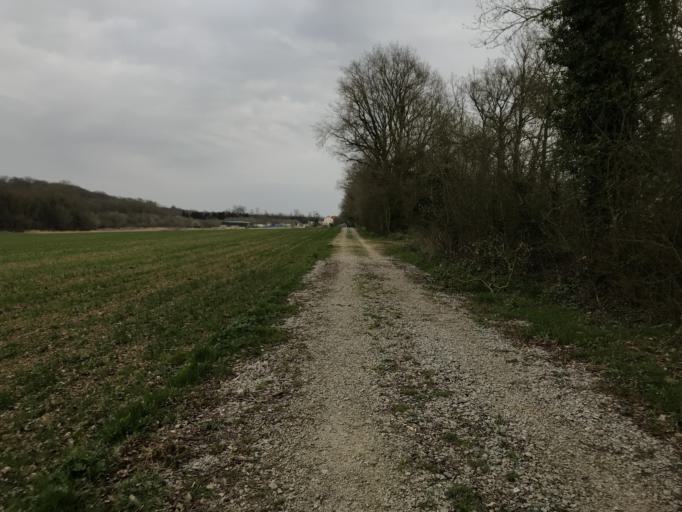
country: FR
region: Ile-de-France
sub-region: Departement de l'Essonne
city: Limours
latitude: 48.6482
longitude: 2.0528
